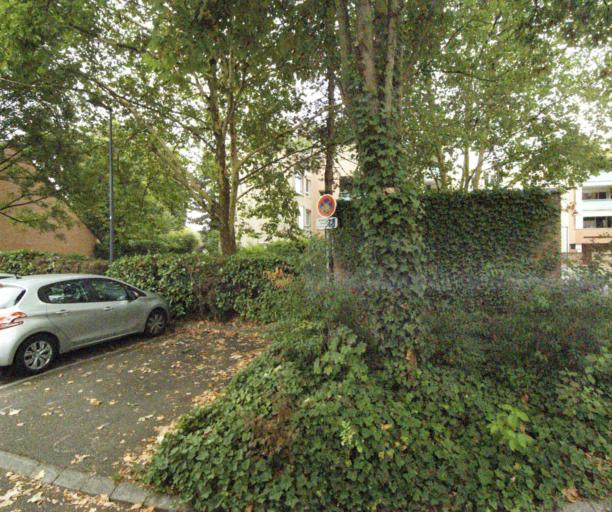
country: FR
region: Nord-Pas-de-Calais
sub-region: Departement du Nord
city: Mons-en-Baroeul
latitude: 50.6313
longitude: 3.1262
